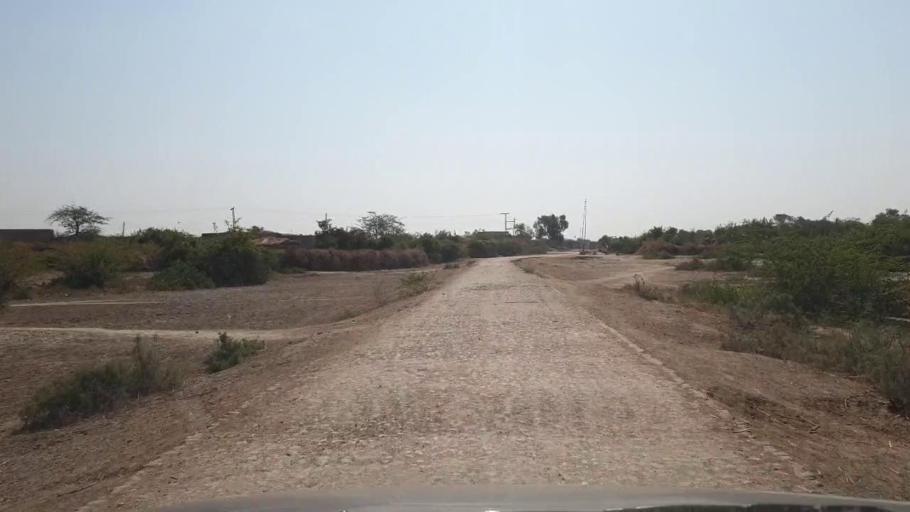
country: PK
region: Sindh
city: Samaro
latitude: 25.2328
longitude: 69.2535
